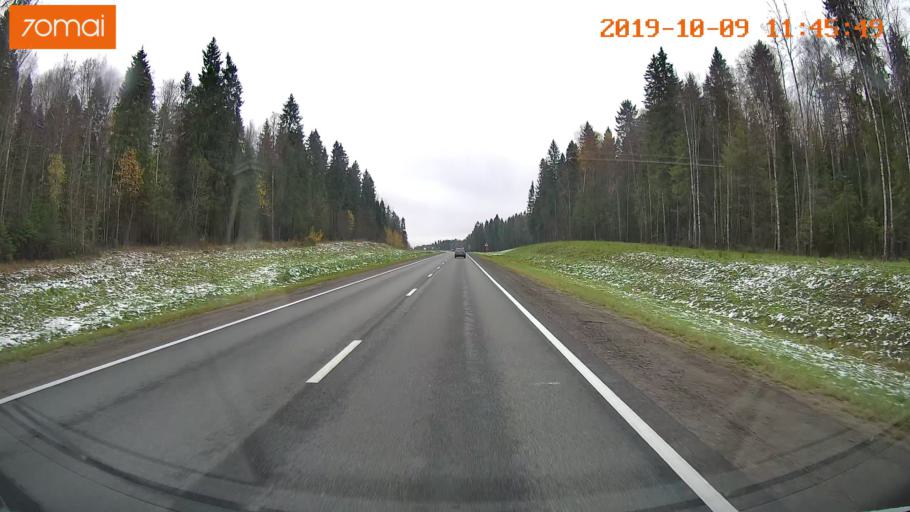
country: RU
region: Vologda
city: Gryazovets
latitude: 58.8630
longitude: 40.1984
